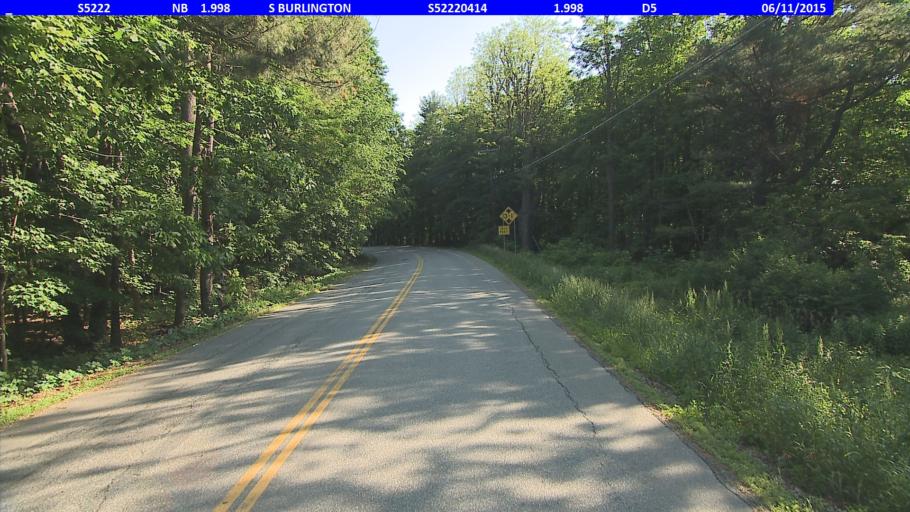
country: US
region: Vermont
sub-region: Chittenden County
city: South Burlington
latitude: 44.4453
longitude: -73.1879
